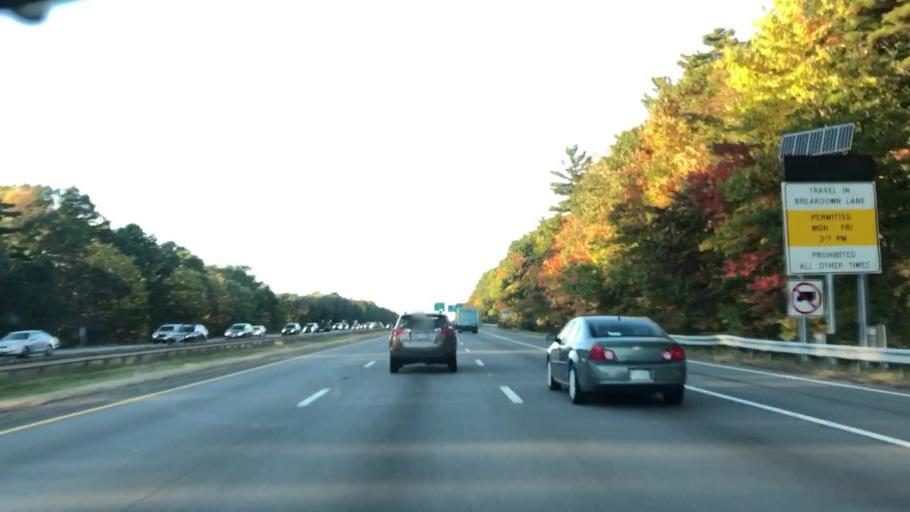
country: US
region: Massachusetts
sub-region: Essex County
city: Andover
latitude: 42.6403
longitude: -71.1833
